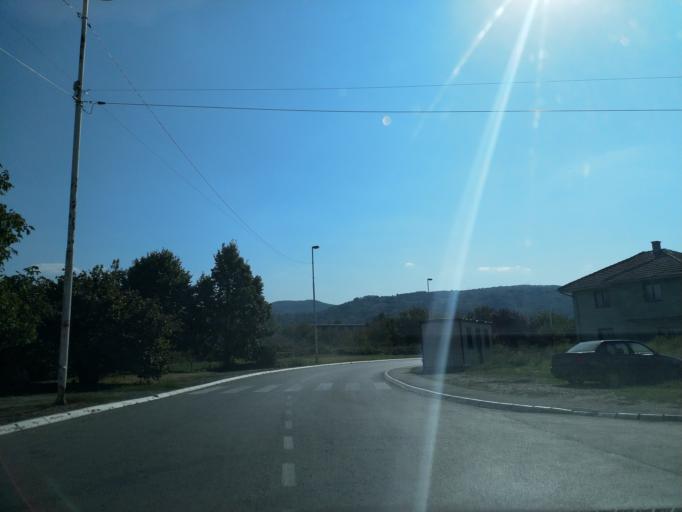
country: RS
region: Central Serbia
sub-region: Rasinski Okrug
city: Trstenik
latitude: 43.6149
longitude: 21.0126
